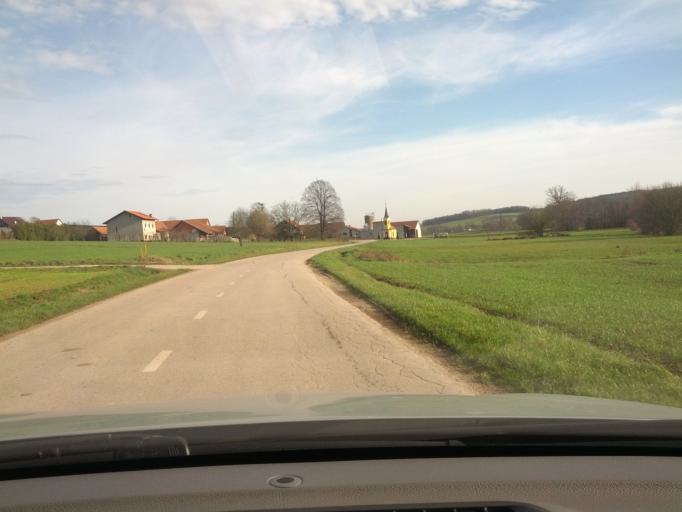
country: SI
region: Sveti Tomaz
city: Sveti Tomaz
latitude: 46.5159
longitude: 16.0945
